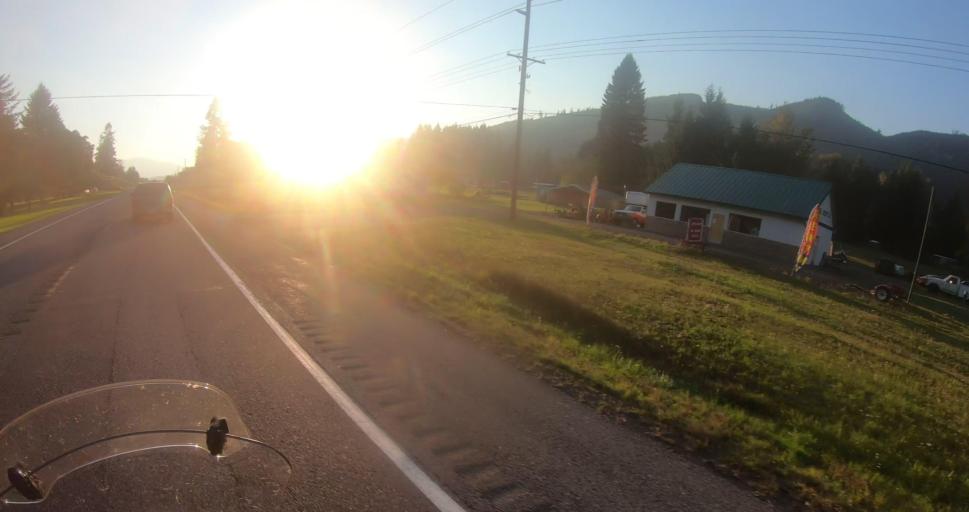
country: US
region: Washington
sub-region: Lewis County
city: Morton
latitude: 46.5350
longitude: -122.1198
